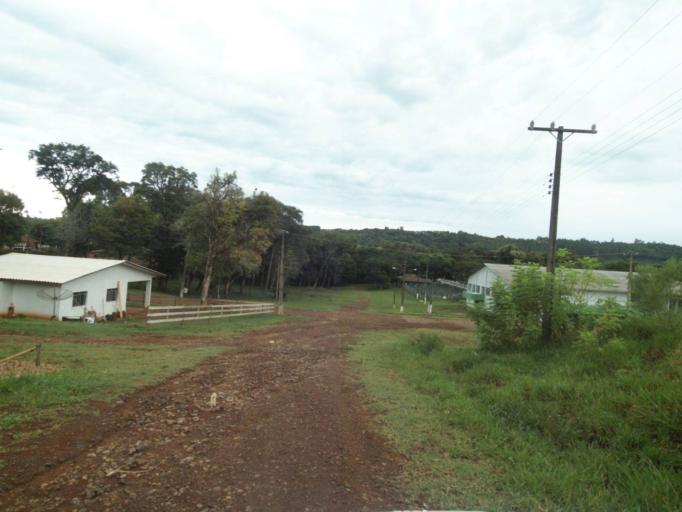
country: BR
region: Parana
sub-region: Guaraniacu
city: Guaraniacu
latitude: -25.1161
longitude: -52.8549
